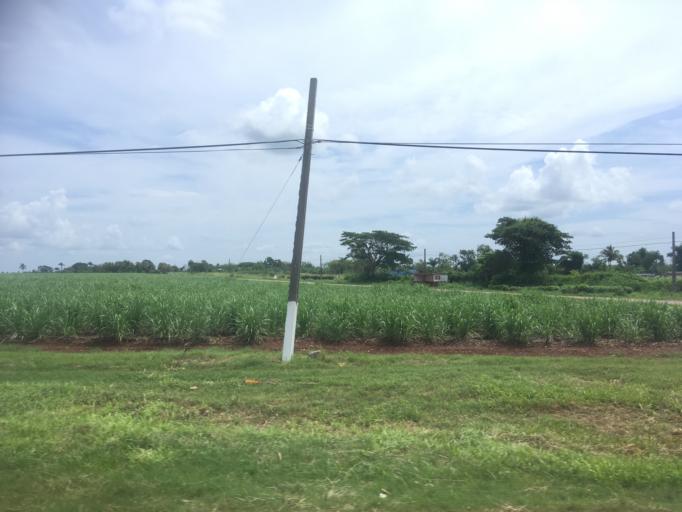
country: CU
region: Matanzas
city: Perico
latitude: 22.7785
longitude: -81.0363
